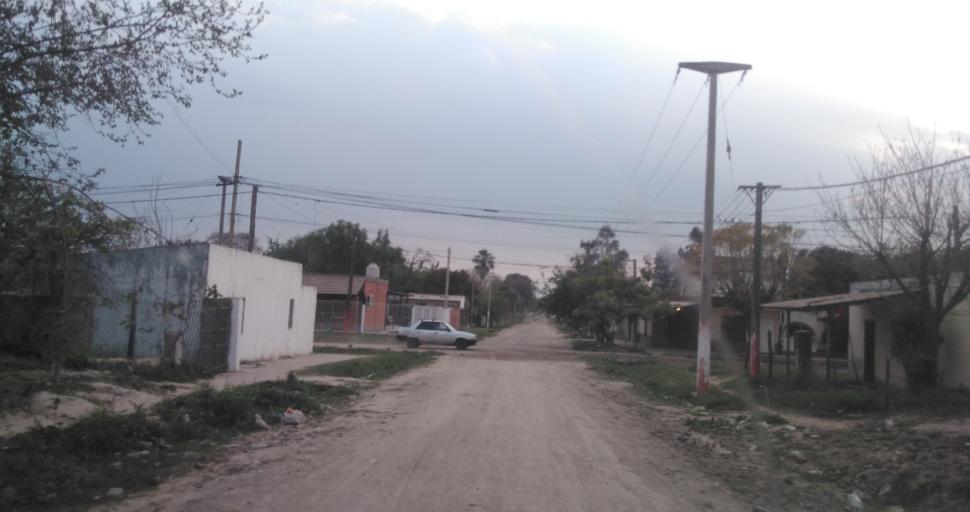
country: AR
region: Chaco
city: Fontana
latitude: -27.4295
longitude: -59.0077
